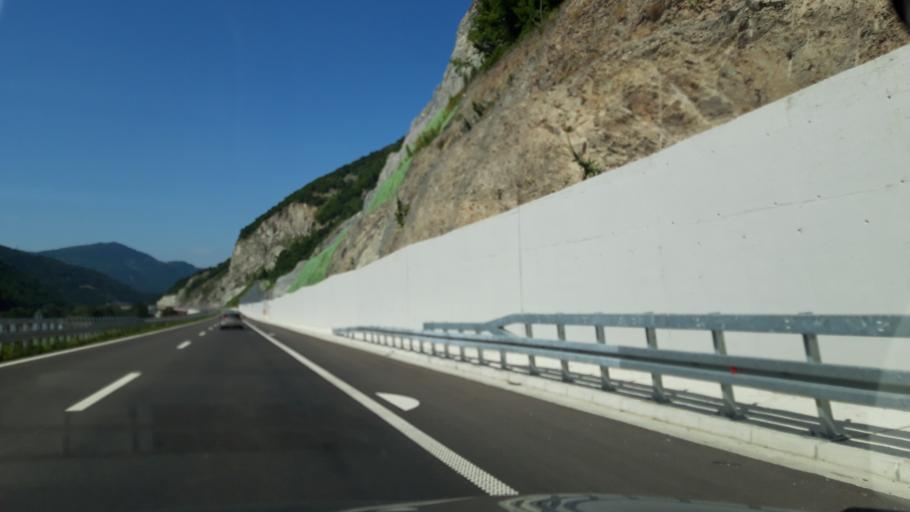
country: RS
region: Central Serbia
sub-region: Pcinjski Okrug
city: Vladicin Han
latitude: 42.7523
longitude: 22.0836
